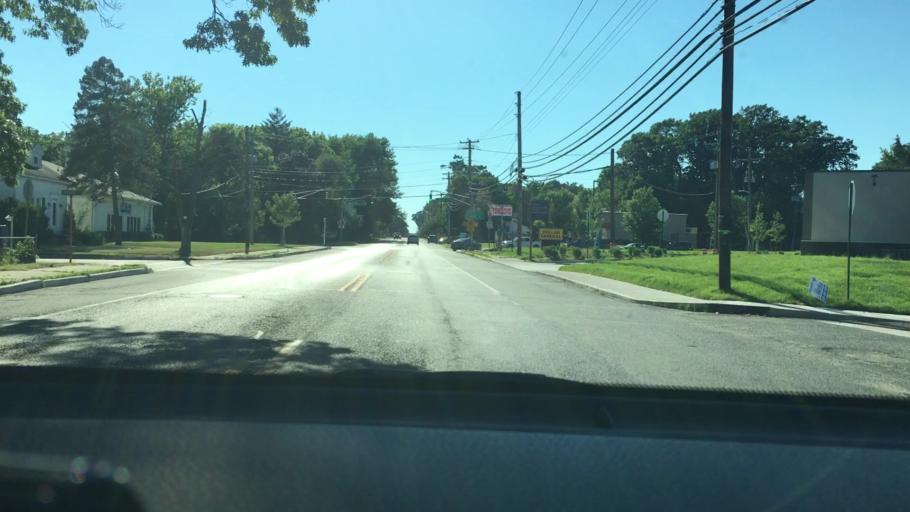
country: US
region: New Jersey
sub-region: Cumberland County
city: Millville
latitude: 39.3983
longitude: -75.0600
